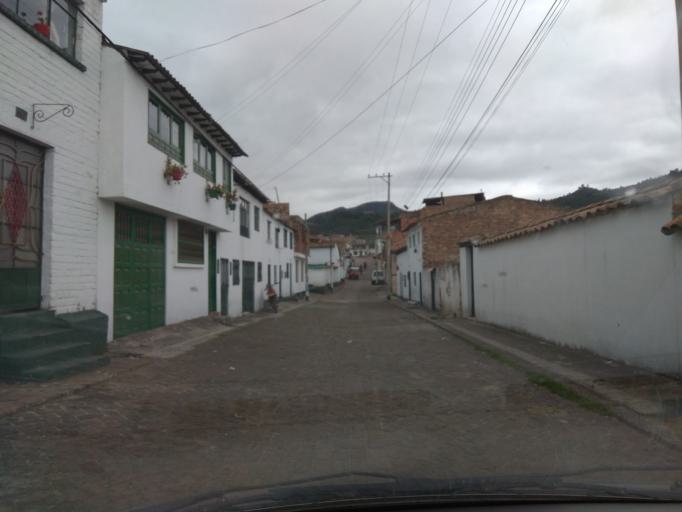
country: CO
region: Boyaca
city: Mongui
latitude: 5.7240
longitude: -72.8495
